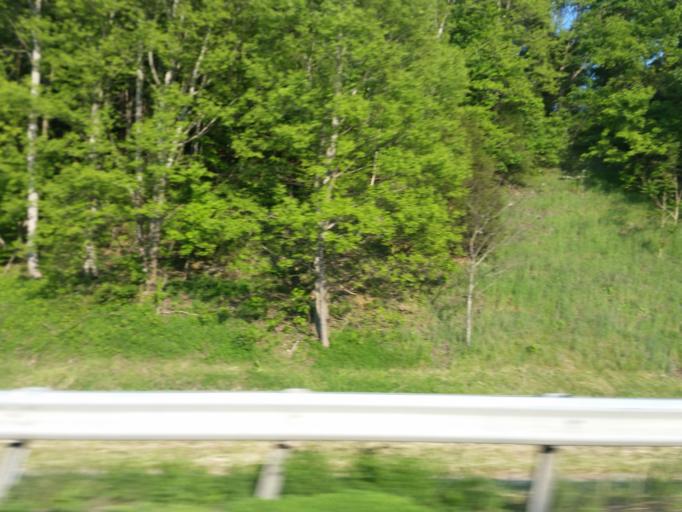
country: US
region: Virginia
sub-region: Russell County
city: Lebanon
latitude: 36.8718
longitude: -82.1115
